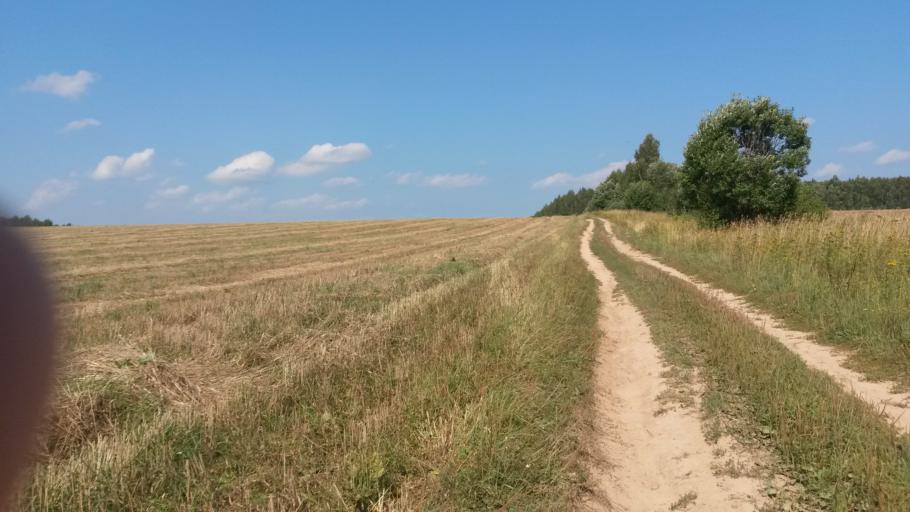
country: RU
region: Jaroslavl
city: Gavrilov-Yam
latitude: 57.3116
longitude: 39.9647
